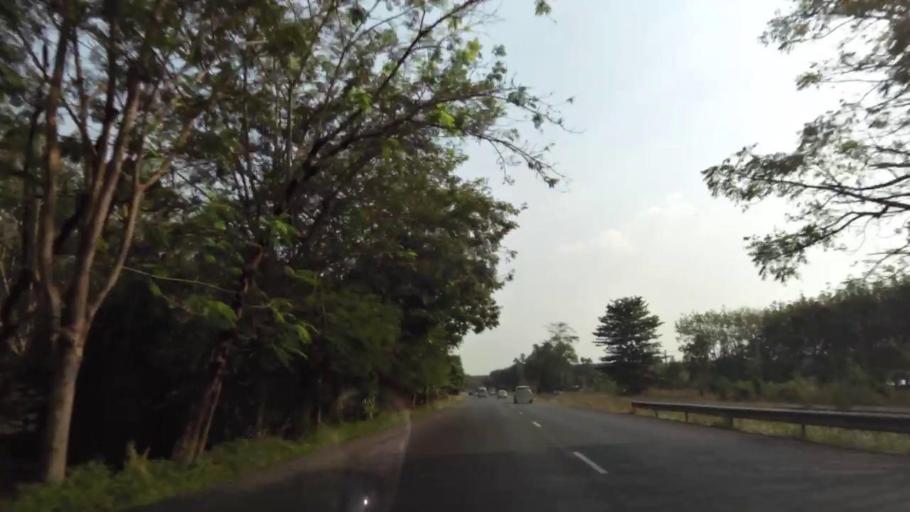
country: TH
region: Rayong
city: Wang Chan
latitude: 12.9672
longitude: 101.4977
